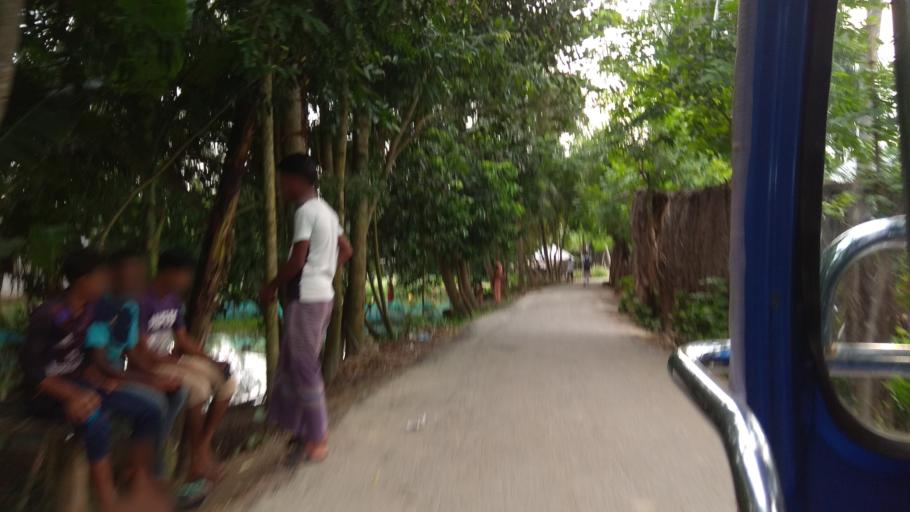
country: BD
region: Khulna
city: Kalia
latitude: 23.0381
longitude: 89.6597
